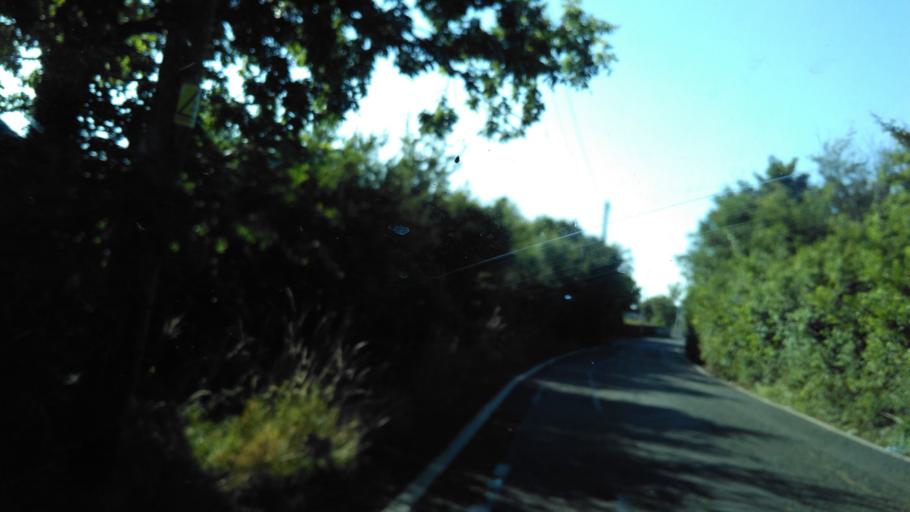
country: GB
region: England
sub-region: Kent
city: Whitstable
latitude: 51.3402
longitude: 1.0070
